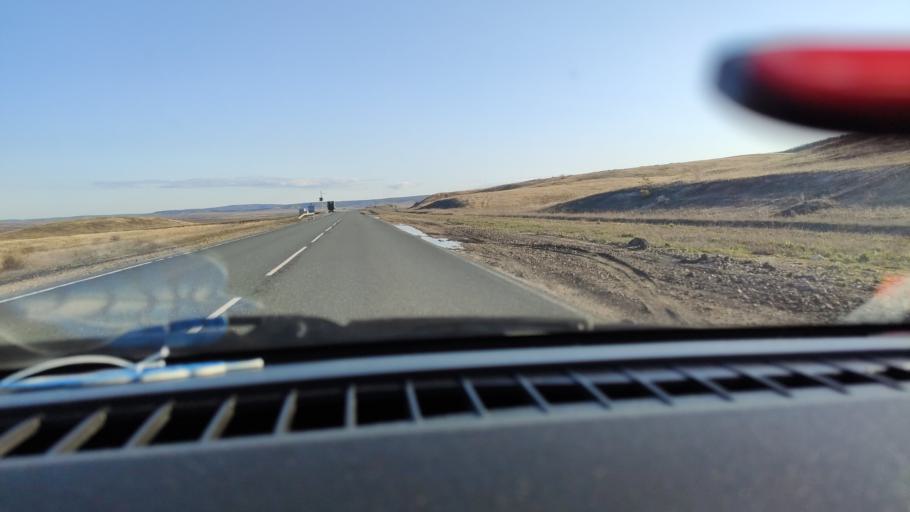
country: RU
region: Saratov
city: Alekseyevka
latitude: 52.3434
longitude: 47.9365
